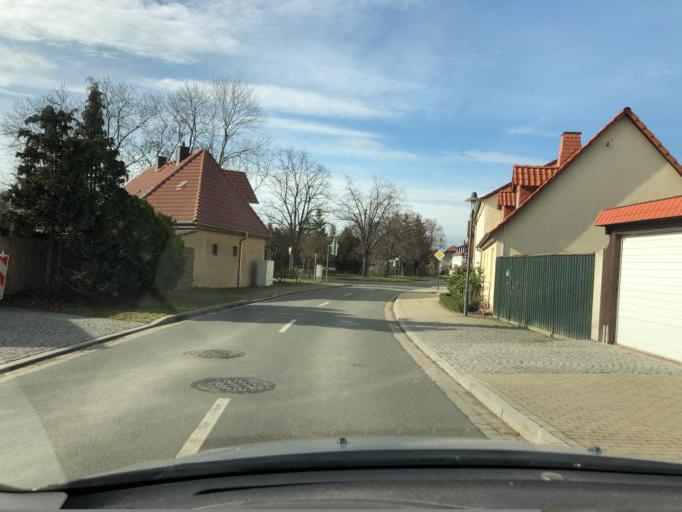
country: DE
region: Thuringia
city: Niederzimmern
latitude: 51.0072
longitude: 11.1923
